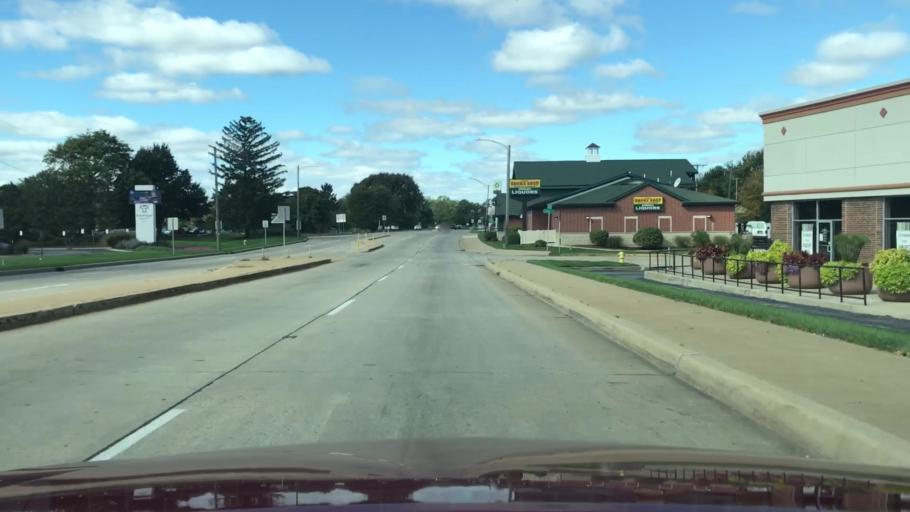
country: US
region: Indiana
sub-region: Lake County
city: Dyer
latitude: 41.4944
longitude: -87.5232
